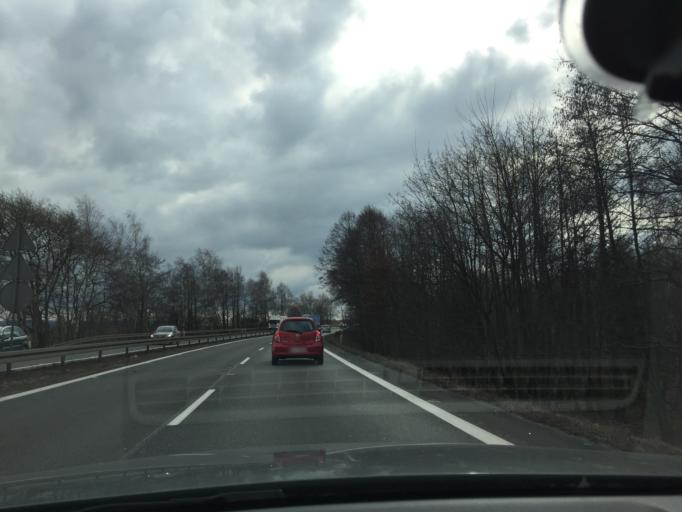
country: PL
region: Silesian Voivodeship
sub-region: Powiat bielski
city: Czechowice-Dziedzice
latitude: 49.8855
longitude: 18.9983
